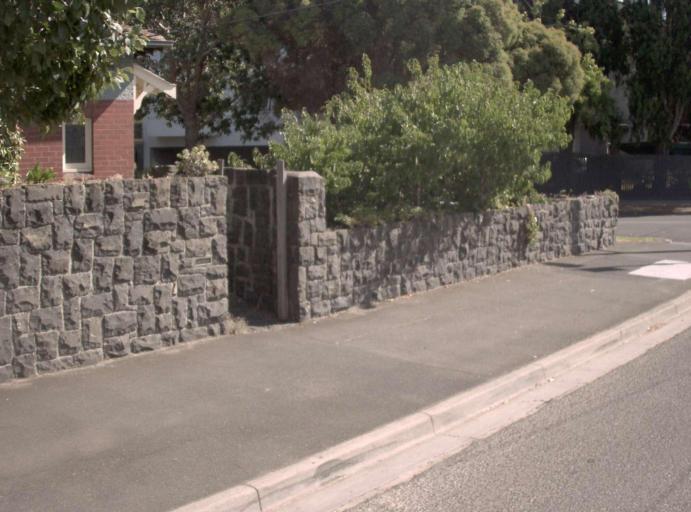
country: AU
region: Victoria
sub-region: Yarra
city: Richmond
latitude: -37.8181
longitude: 145.0185
